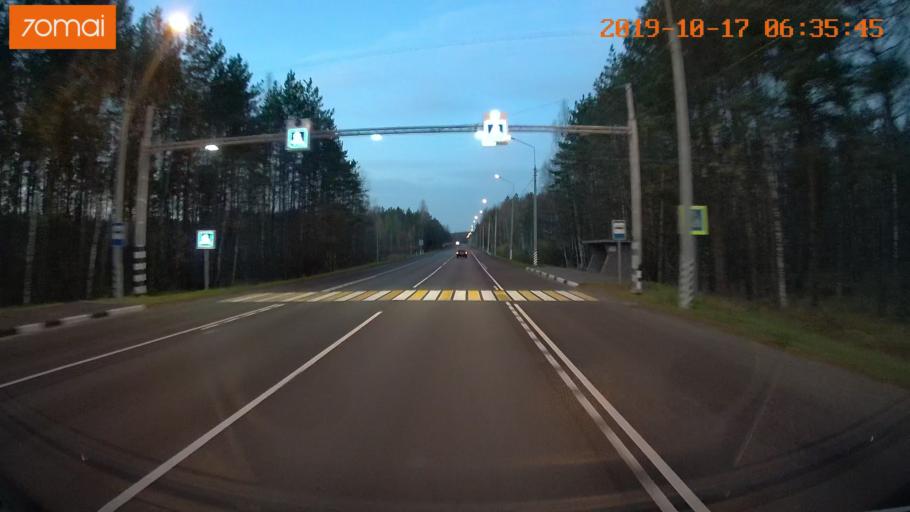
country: RU
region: Ivanovo
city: Novoye Leushino
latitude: 56.6892
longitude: 40.6166
